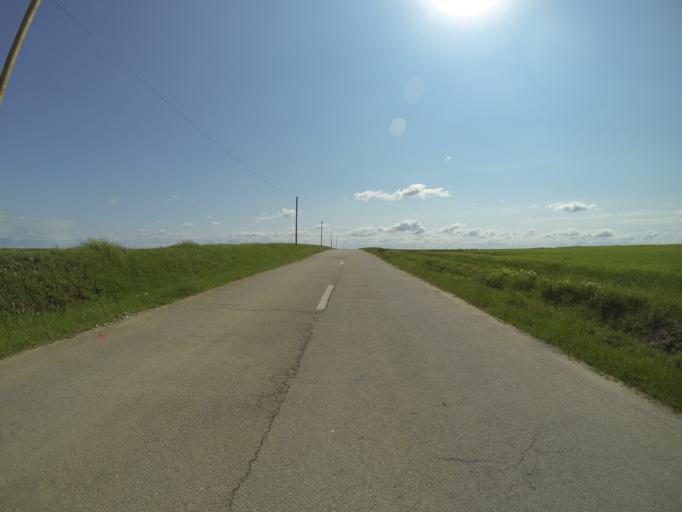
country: RO
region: Dolj
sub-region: Comuna Orodelu
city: Orodelu
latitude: 44.2440
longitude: 23.2211
